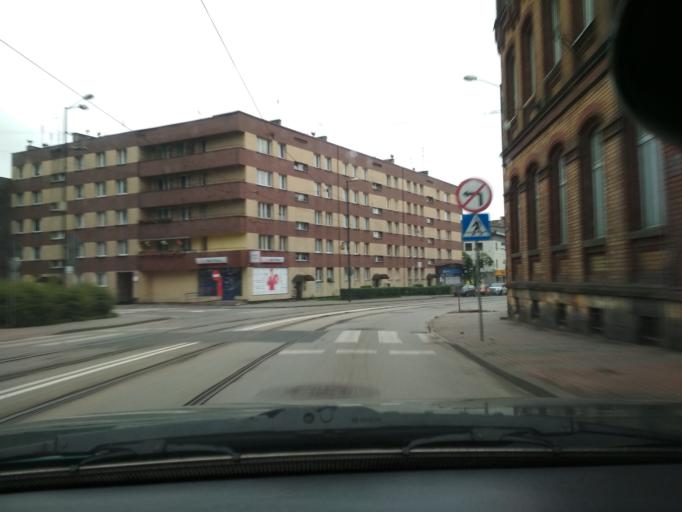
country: PL
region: Silesian Voivodeship
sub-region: Swietochlowice
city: Swietochlowice
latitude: 50.2938
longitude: 18.9170
